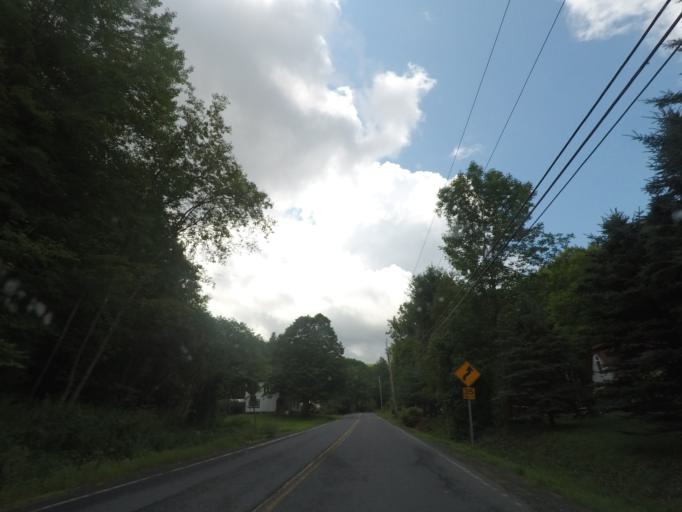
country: US
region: Massachusetts
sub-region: Berkshire County
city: Williamstown
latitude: 42.6877
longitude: -73.3814
